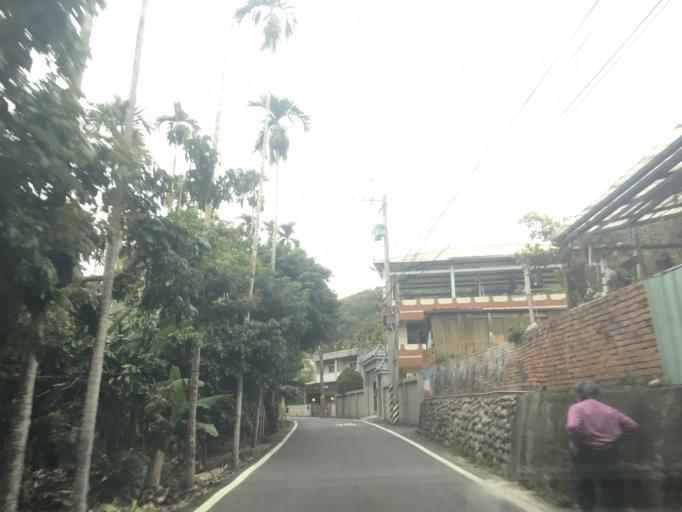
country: TW
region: Taiwan
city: Zhongxing New Village
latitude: 24.0384
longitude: 120.7196
